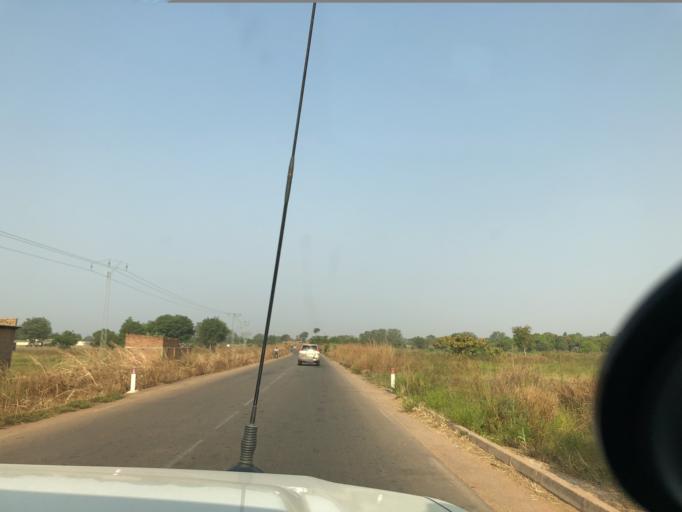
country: TD
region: Logone Occidental
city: Moundou
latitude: 8.5793
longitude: 16.0339
